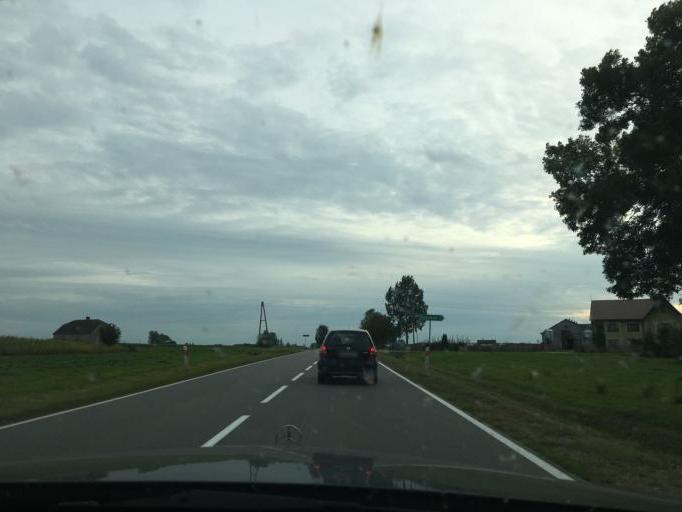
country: PL
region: Masovian Voivodeship
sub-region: Powiat ostrolecki
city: Czerwin
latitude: 52.9319
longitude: 21.8823
